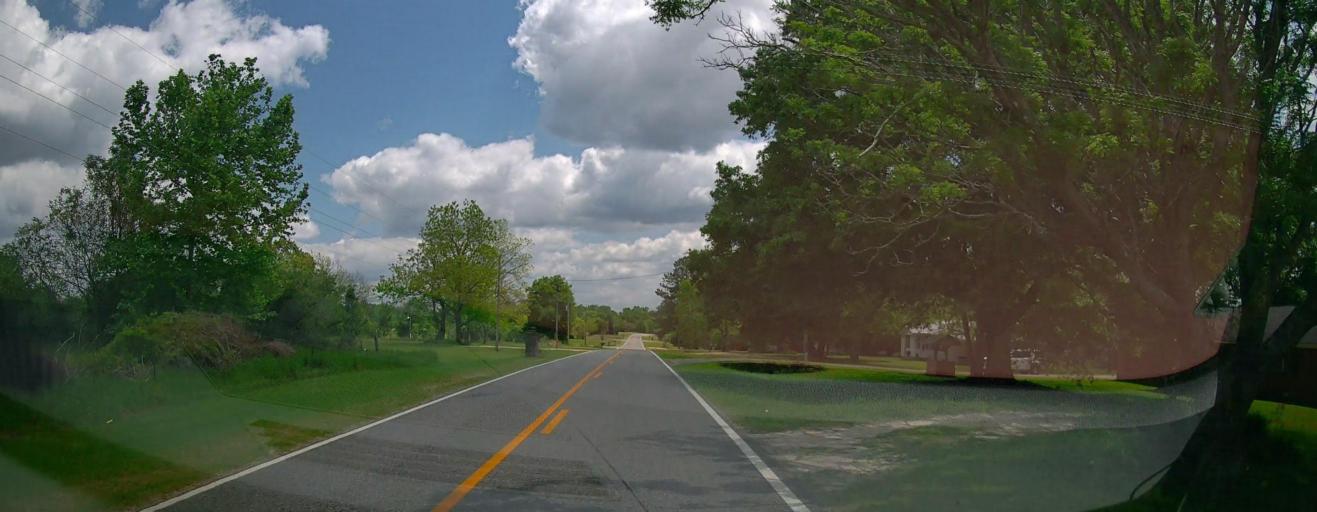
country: US
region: Georgia
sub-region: Laurens County
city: East Dublin
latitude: 32.5591
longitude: -82.8198
